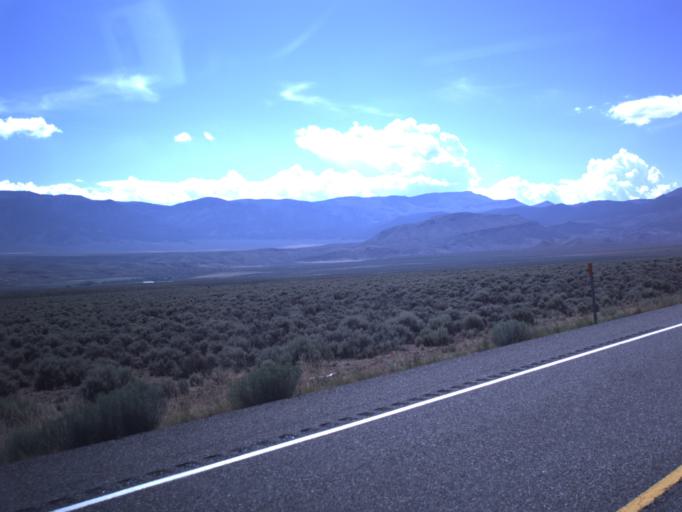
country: US
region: Utah
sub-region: Piute County
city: Junction
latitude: 38.3803
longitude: -112.2280
